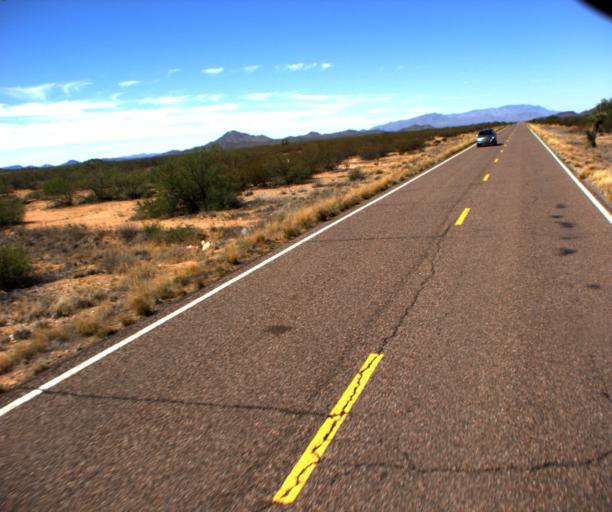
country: US
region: Arizona
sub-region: Yavapai County
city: Congress
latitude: 34.0699
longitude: -113.0340
